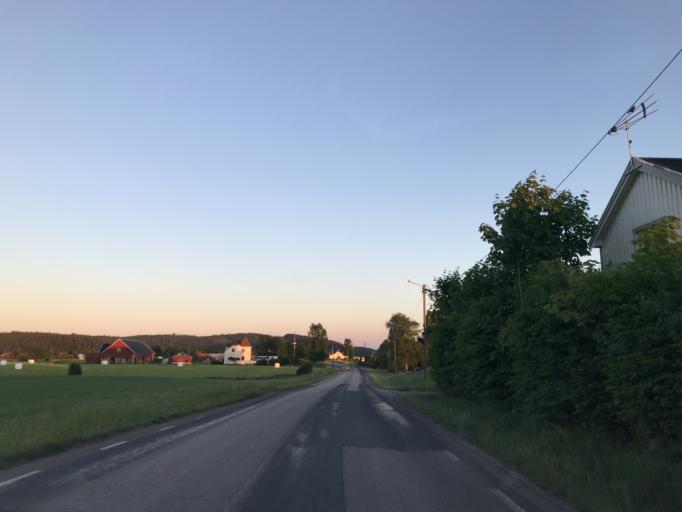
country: SE
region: Vaestra Goetaland
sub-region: Marks Kommun
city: Horred
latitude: 57.4355
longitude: 12.5162
